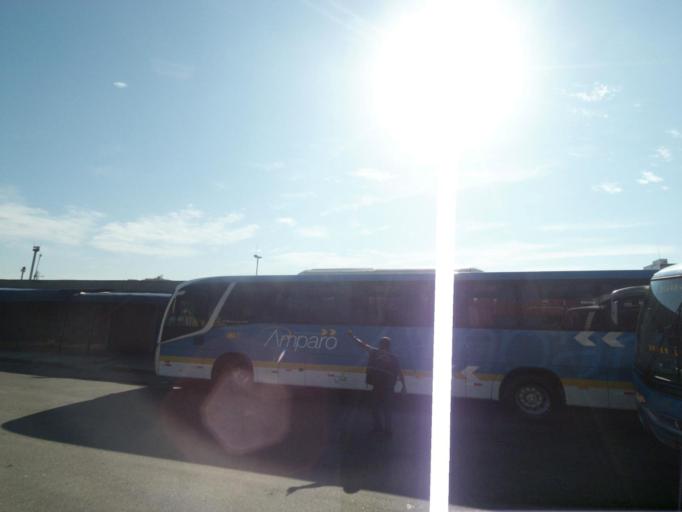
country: BR
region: Rio de Janeiro
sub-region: Niteroi
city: Niteroi
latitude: -22.8904
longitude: -43.1268
